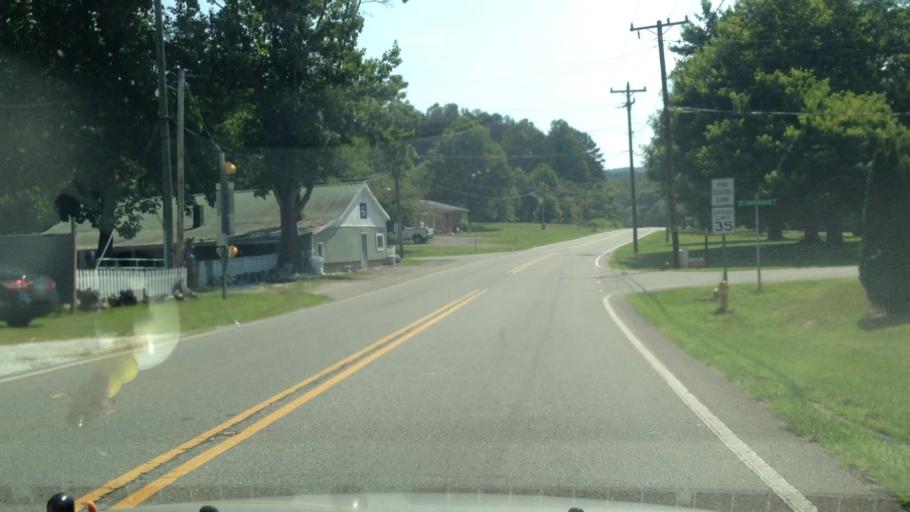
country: US
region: North Carolina
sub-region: Surry County
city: Flat Rock
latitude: 36.5137
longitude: -80.5651
